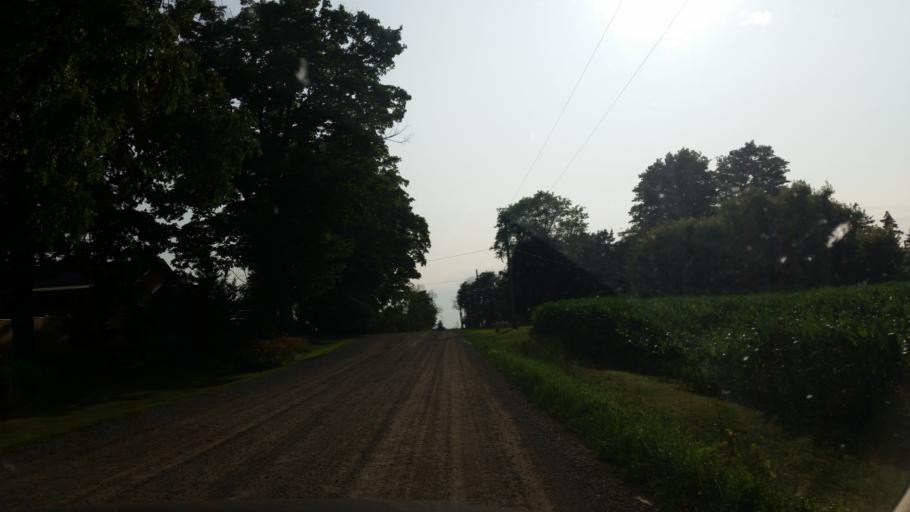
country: CA
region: Ontario
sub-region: Oxford County
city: Woodstock
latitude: 43.0462
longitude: -80.6136
